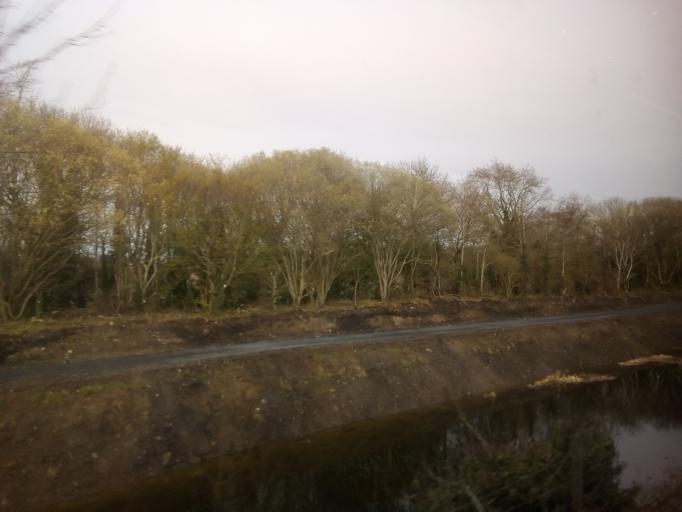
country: IE
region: Leinster
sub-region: Kildare
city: Leixlip
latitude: 53.3734
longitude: -6.5282
